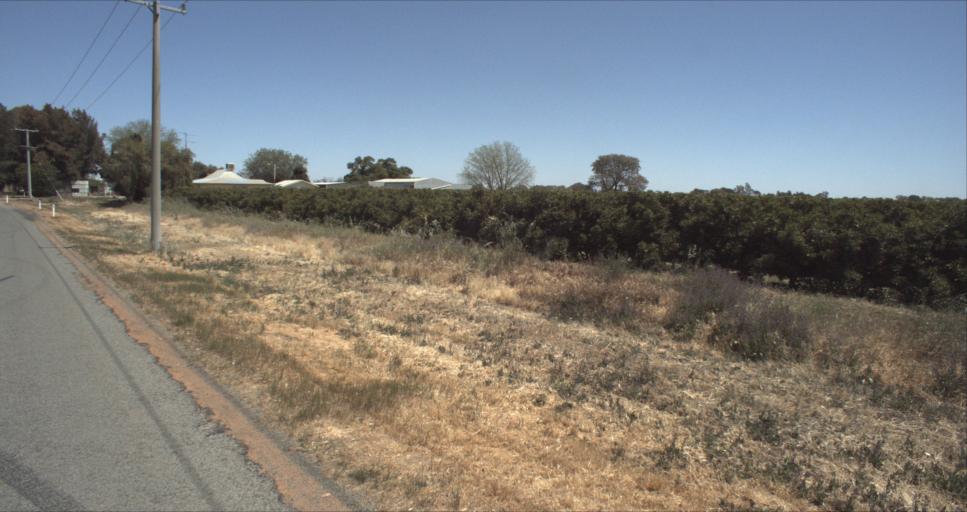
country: AU
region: New South Wales
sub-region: Leeton
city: Leeton
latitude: -34.5366
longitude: 146.3963
